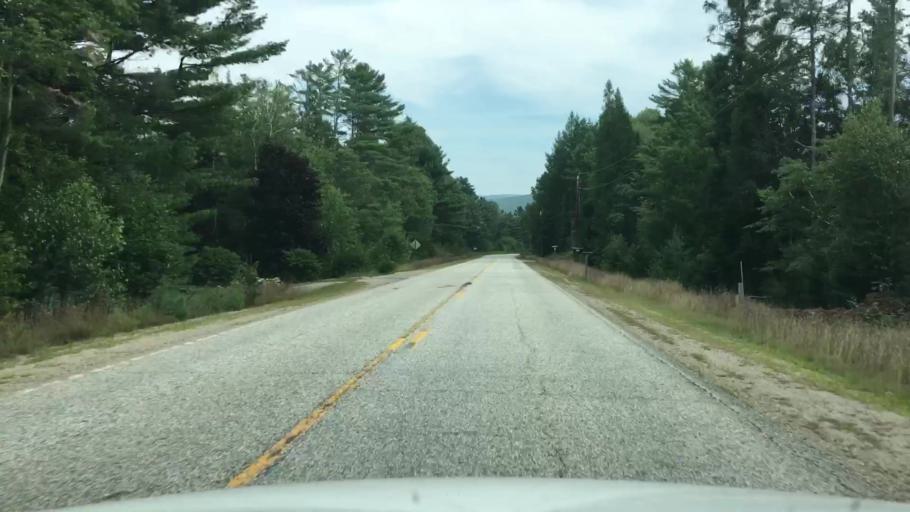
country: US
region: Maine
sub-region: Oxford County
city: Rumford
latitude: 44.6153
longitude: -70.7414
